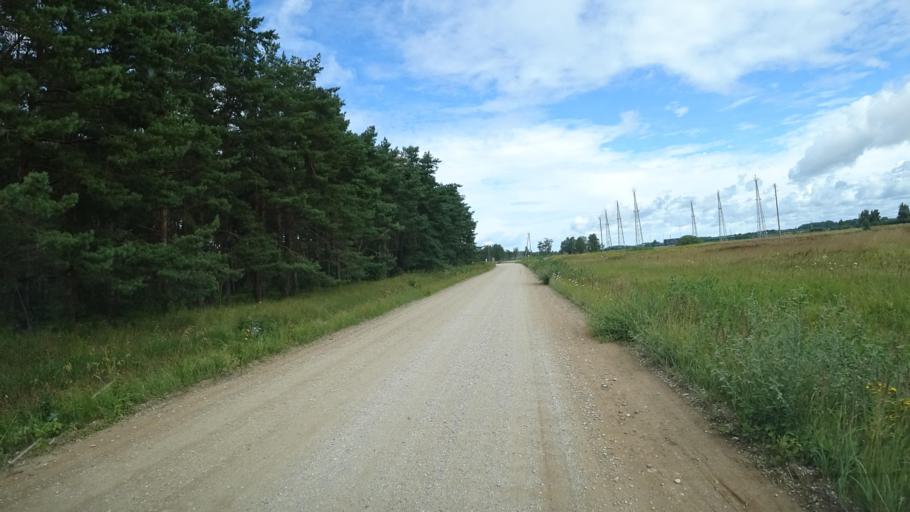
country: LV
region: Liepaja
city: Vec-Liepaja
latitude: 56.6379
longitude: 21.0454
